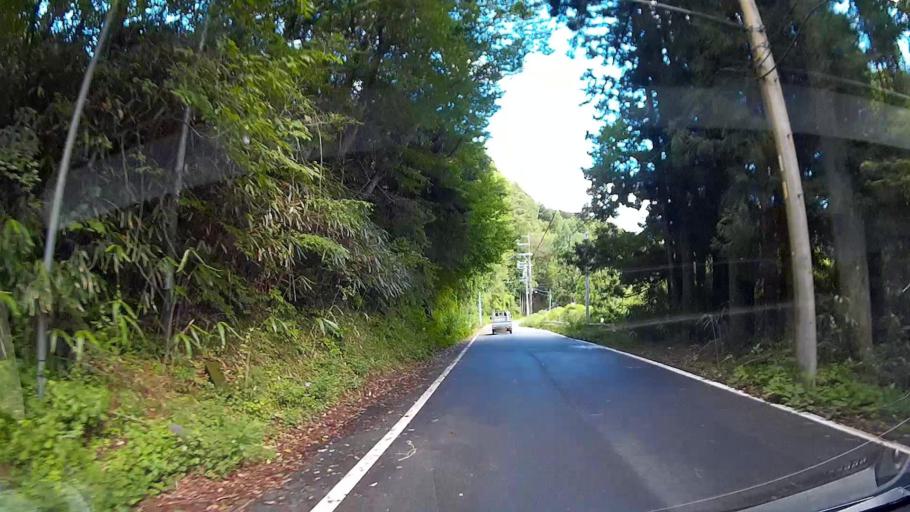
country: JP
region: Shizuoka
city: Shizuoka-shi
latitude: 35.2196
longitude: 138.2320
